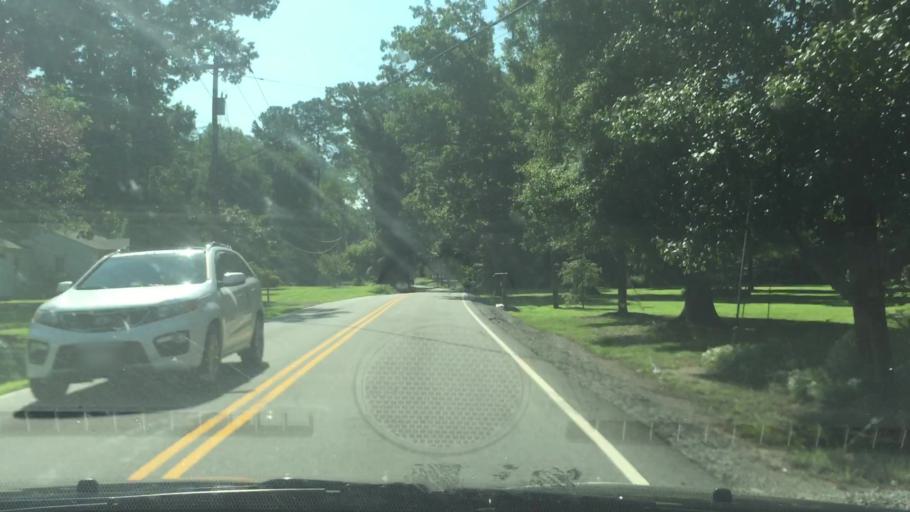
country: US
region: Virginia
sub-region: Hanover County
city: Ashland
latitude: 37.7409
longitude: -77.4617
